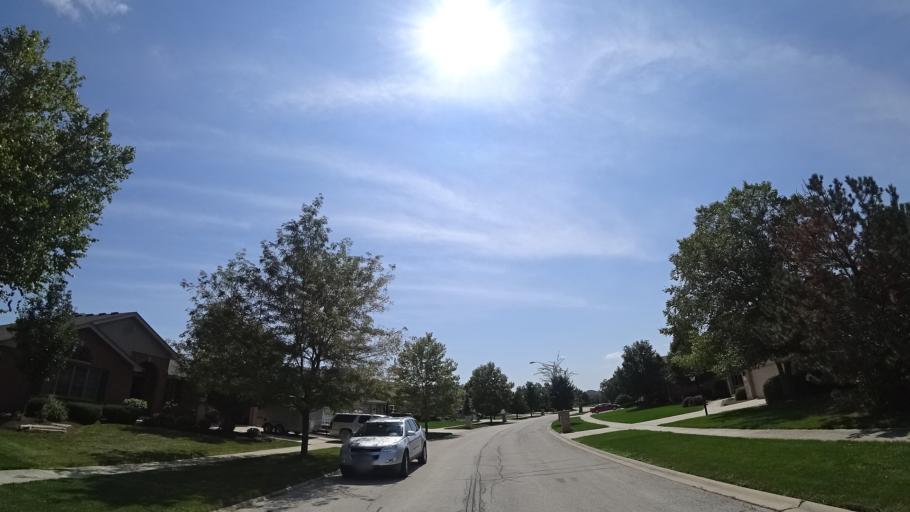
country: US
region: Illinois
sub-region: Cook County
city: Orland Hills
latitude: 41.5678
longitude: -87.8296
